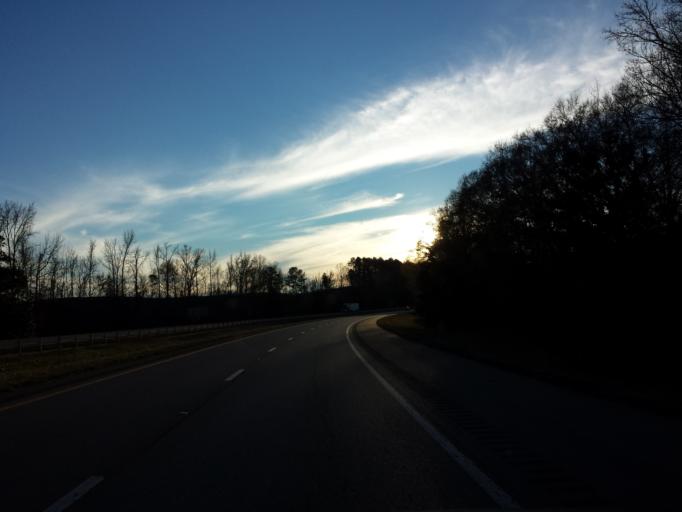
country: US
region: Alabama
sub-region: Sumter County
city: York
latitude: 32.4145
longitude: -88.4608
